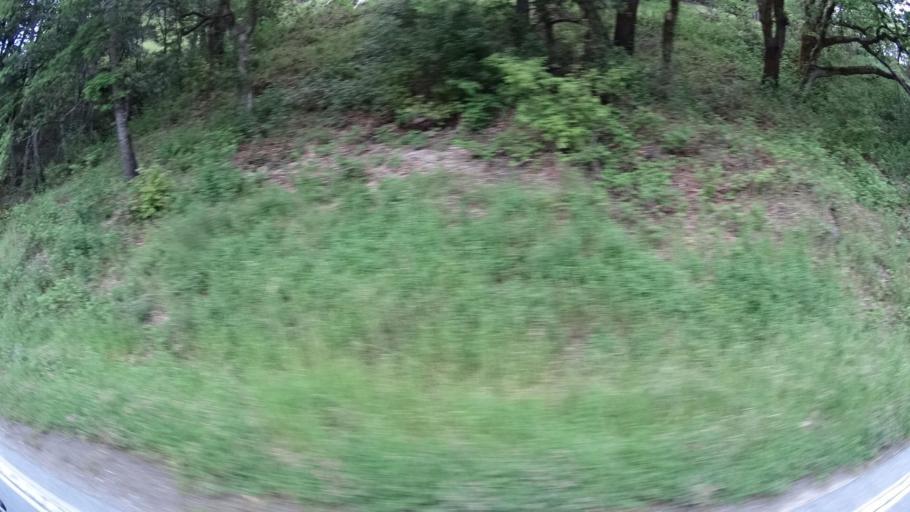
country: US
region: California
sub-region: Humboldt County
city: Willow Creek
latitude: 41.1929
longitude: -123.7168
